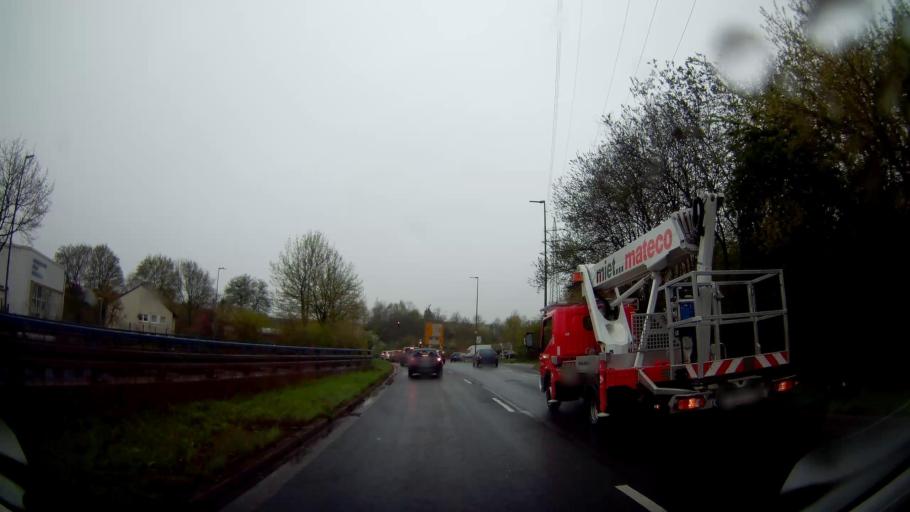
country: DE
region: North Rhine-Westphalia
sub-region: Regierungsbezirk Arnsberg
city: Dortmund
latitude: 51.5249
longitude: 7.4238
